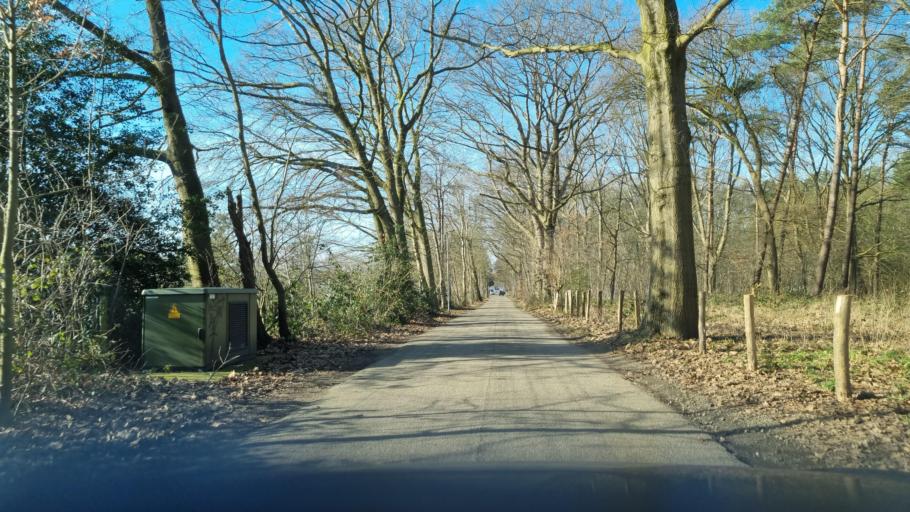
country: DE
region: North Rhine-Westphalia
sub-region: Regierungsbezirk Dusseldorf
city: Kleve
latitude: 51.7586
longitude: 6.1084
